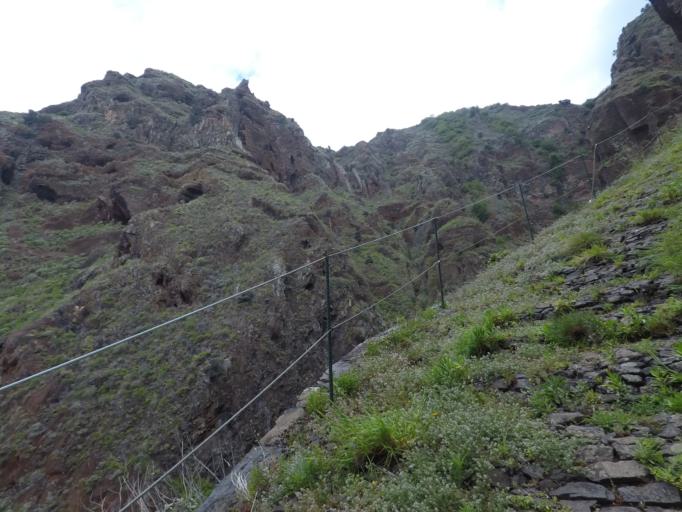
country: PT
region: Madeira
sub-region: Calheta
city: Faja da Ovelha
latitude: 32.7543
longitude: -17.2218
